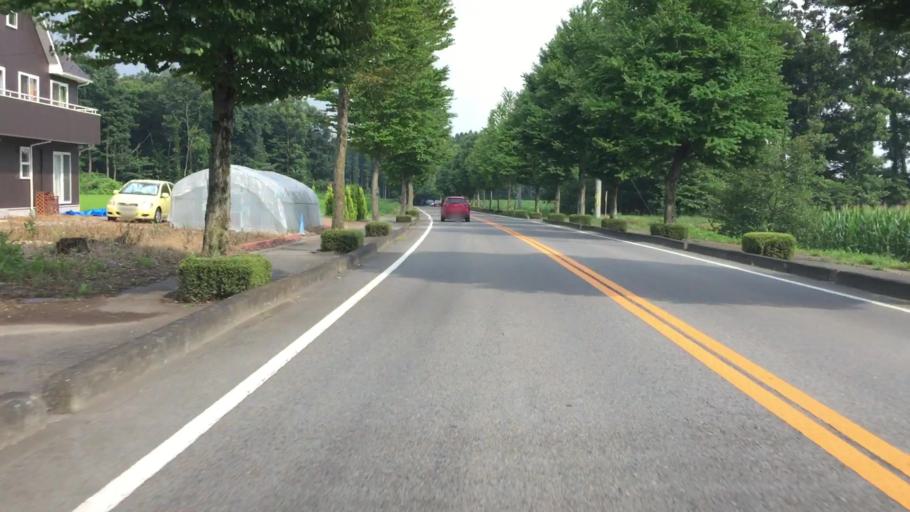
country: JP
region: Tochigi
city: Kuroiso
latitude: 36.9792
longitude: 139.9643
